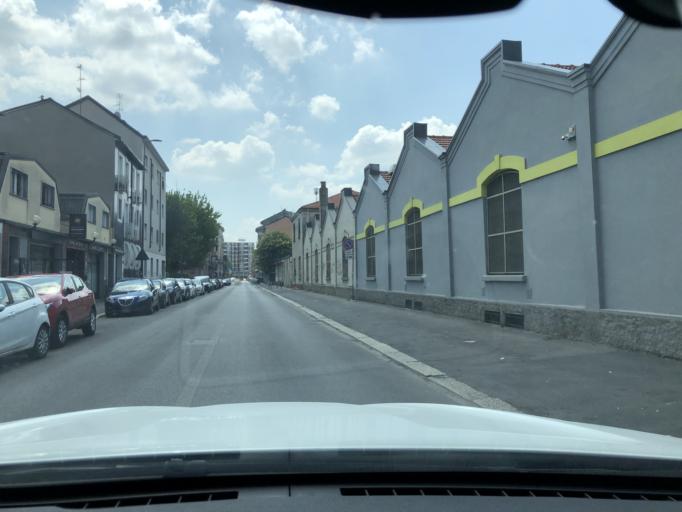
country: IT
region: Lombardy
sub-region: Citta metropolitana di Milano
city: Milano
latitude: 45.5006
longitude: 9.1711
